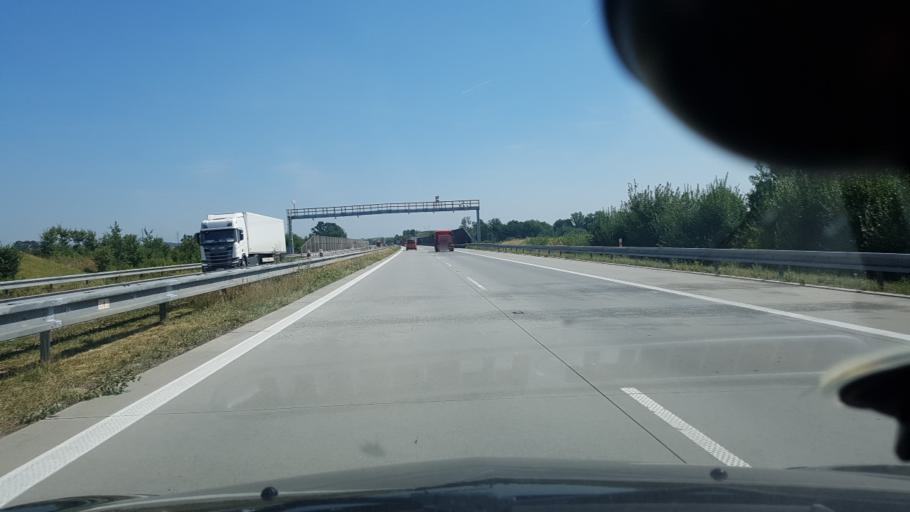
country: CZ
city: Kunin
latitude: 49.6963
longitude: 17.9729
